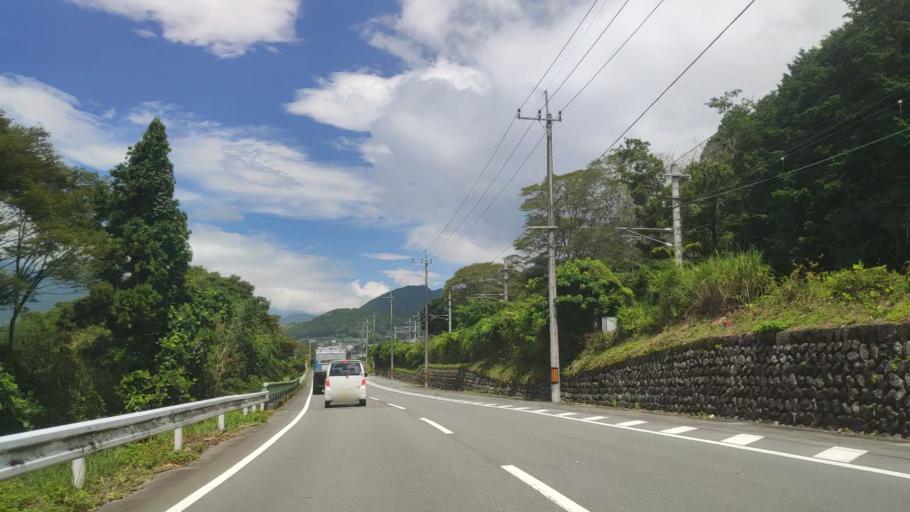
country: JP
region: Shizuoka
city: Fujinomiya
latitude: 35.2715
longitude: 138.4708
